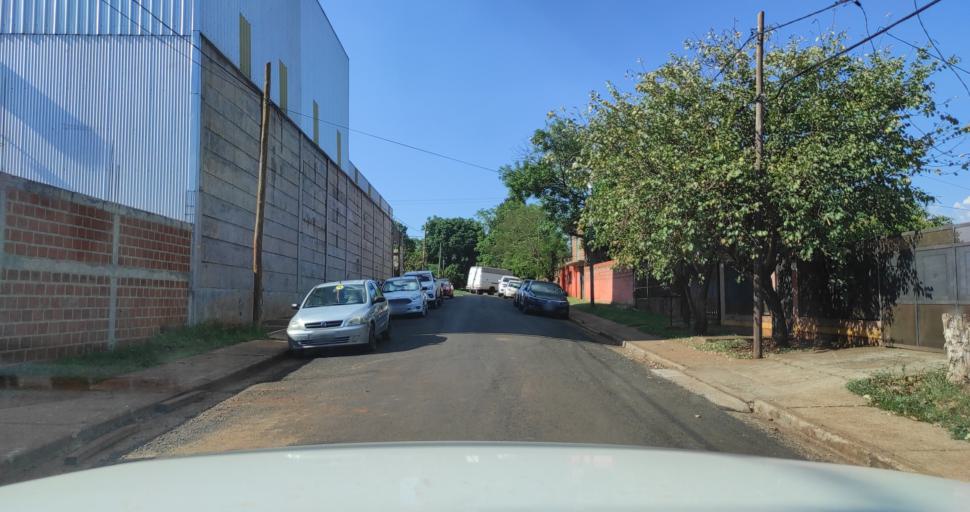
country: AR
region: Misiones
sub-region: Departamento de Capital
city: Posadas
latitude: -27.4135
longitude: -55.9257
